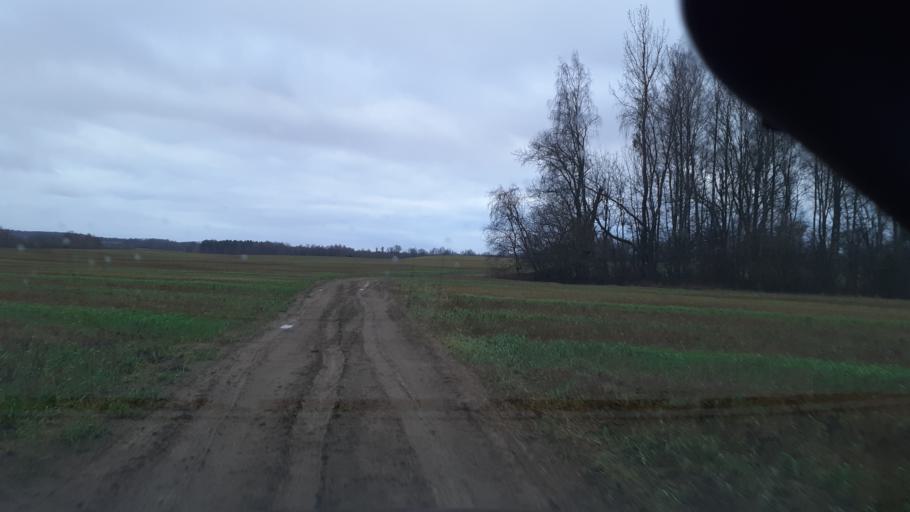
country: LV
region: Kuldigas Rajons
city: Kuldiga
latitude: 56.8842
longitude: 21.7699
